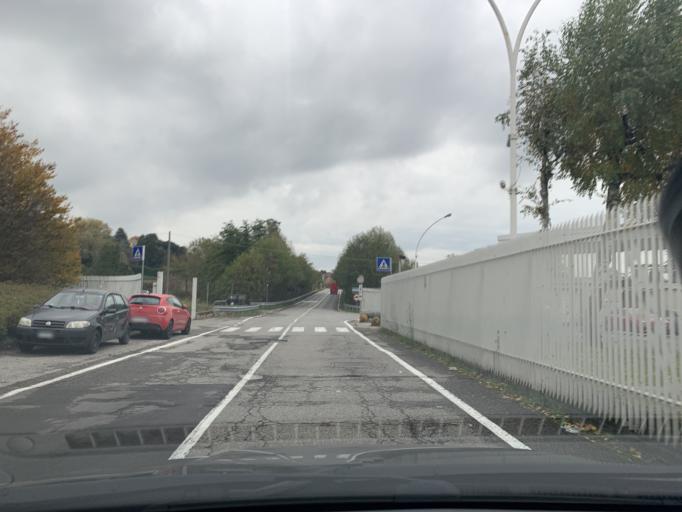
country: IT
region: Lombardy
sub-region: Provincia di Como
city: Grandate
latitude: 45.7658
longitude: 9.0643
